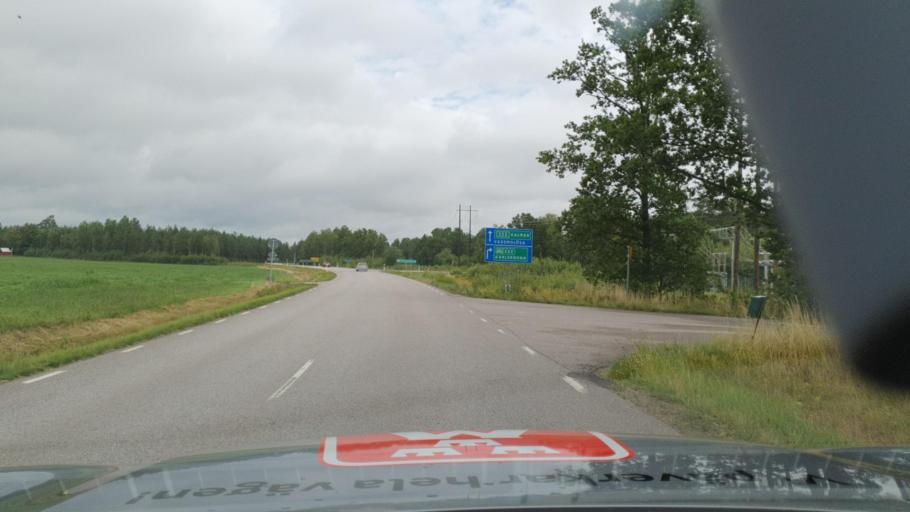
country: SE
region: Kalmar
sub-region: Kalmar Kommun
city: Ljungbyholm
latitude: 56.5885
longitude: 16.1156
